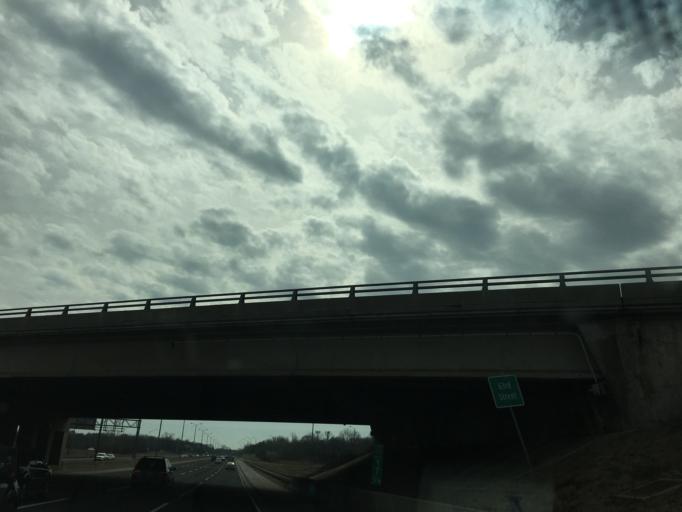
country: US
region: Illinois
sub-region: DuPage County
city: Woodridge
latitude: 41.7725
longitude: -88.0463
